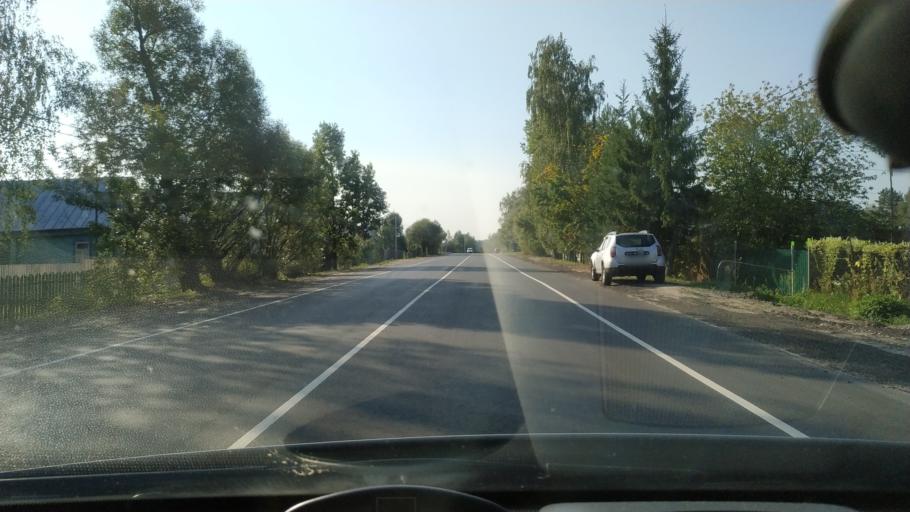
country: RU
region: Moskovskaya
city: Misheronskiy
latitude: 55.6507
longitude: 39.7551
